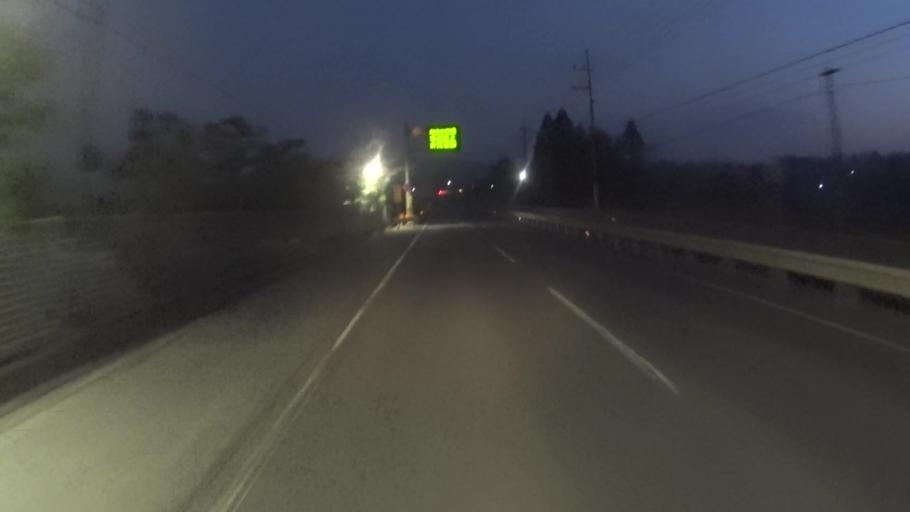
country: JP
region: Kyoto
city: Ayabe
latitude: 35.1774
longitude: 135.4223
